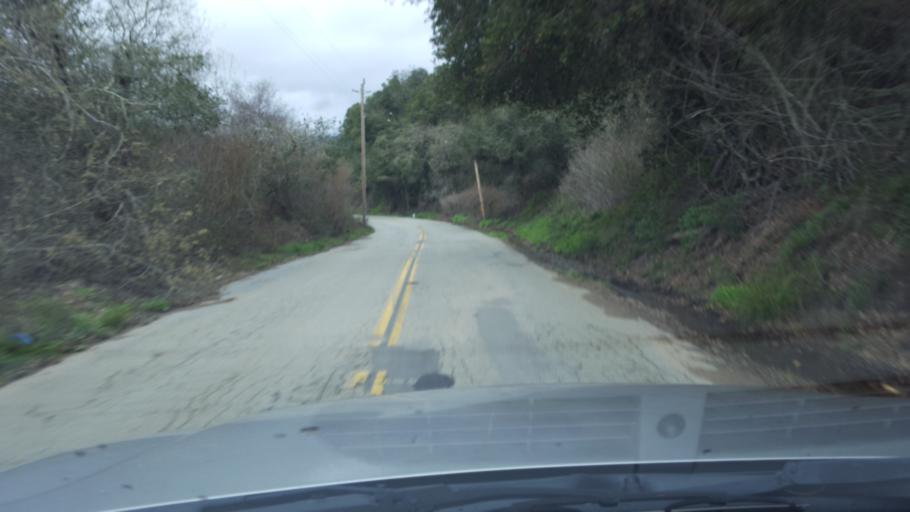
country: US
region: California
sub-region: Santa Cruz County
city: Interlaken
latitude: 36.9941
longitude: -121.7360
